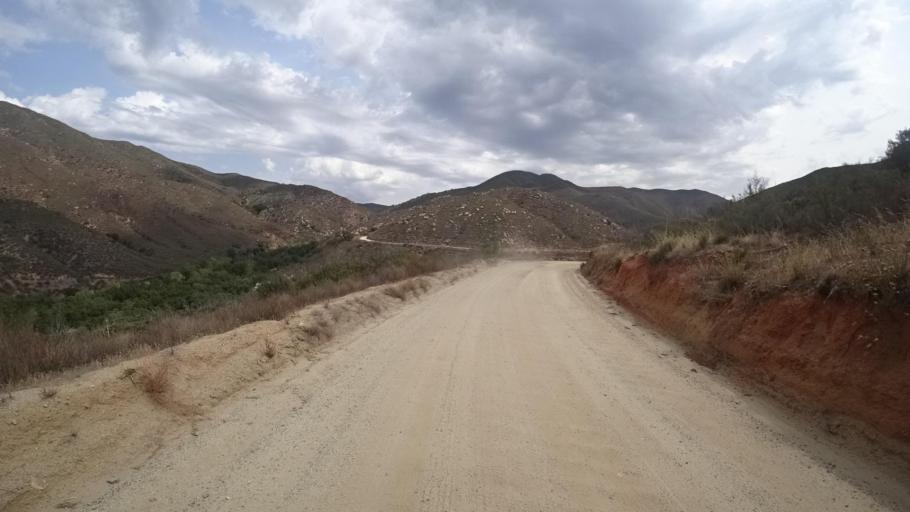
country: US
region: California
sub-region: San Diego County
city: Ramona
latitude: 33.1238
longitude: -116.8049
